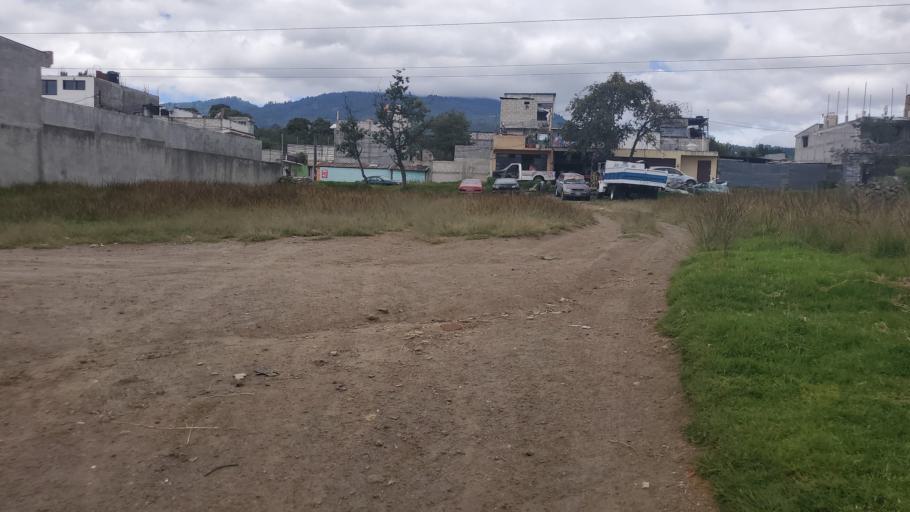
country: GT
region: Quetzaltenango
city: Quetzaltenango
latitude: 14.8353
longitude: -91.5369
